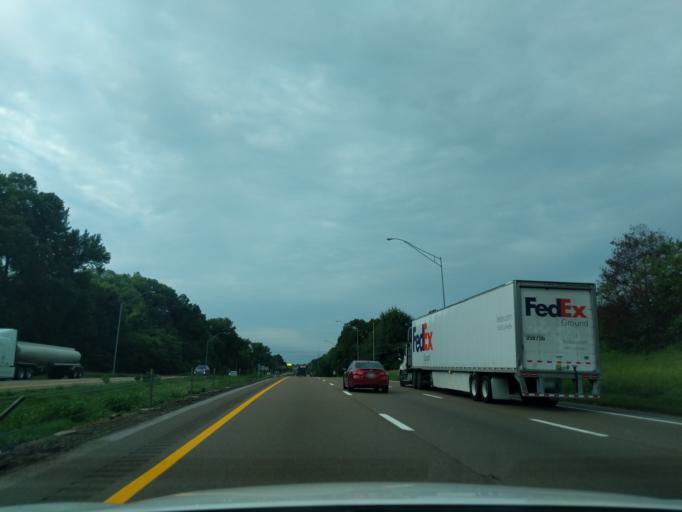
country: US
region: Tennessee
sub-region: Shelby County
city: New South Memphis
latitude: 35.0933
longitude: -90.0765
